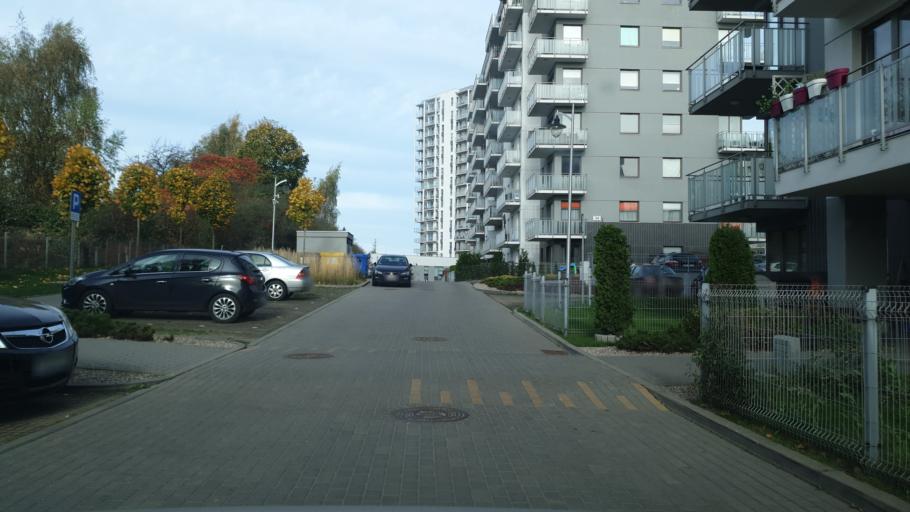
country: PL
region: Pomeranian Voivodeship
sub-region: Powiat gdanski
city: Kowale
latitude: 54.3490
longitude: 18.5863
